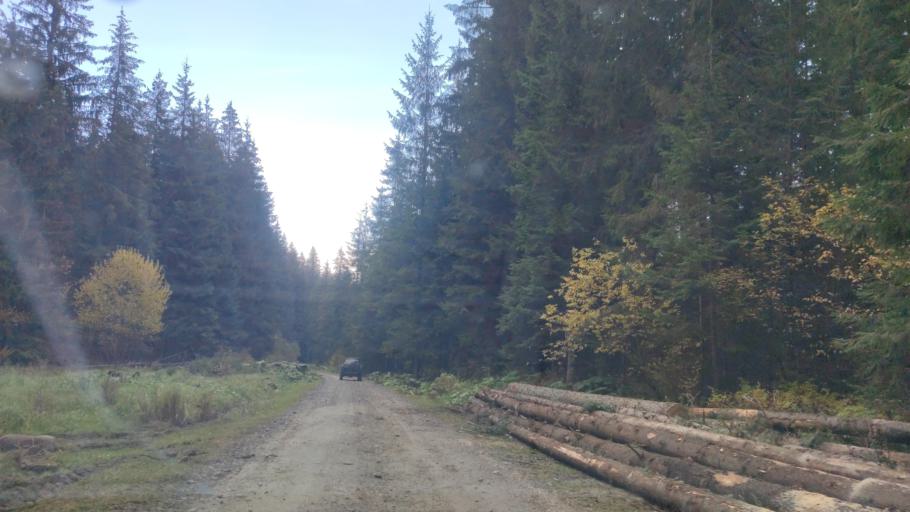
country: RO
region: Harghita
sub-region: Comuna Madaras
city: Madaras
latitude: 46.4793
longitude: 25.6547
